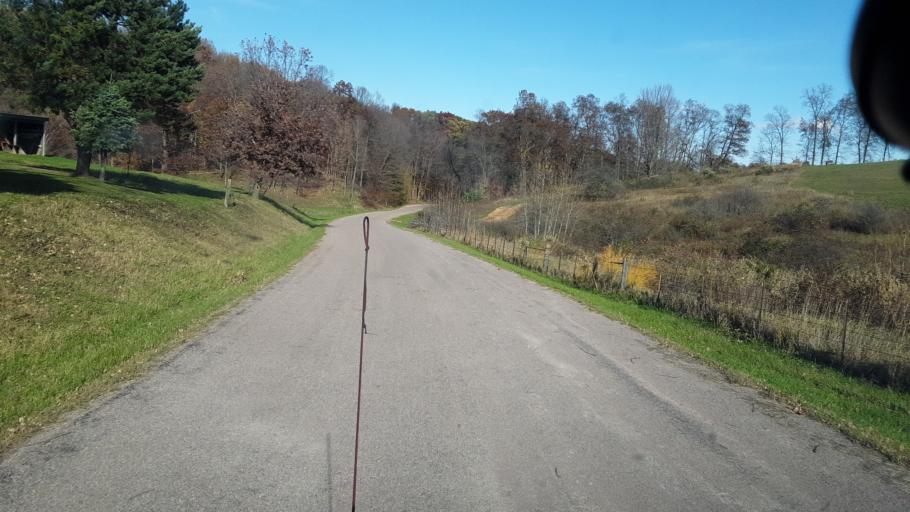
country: US
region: Wisconsin
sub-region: Vernon County
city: Hillsboro
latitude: 43.6558
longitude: -90.4552
